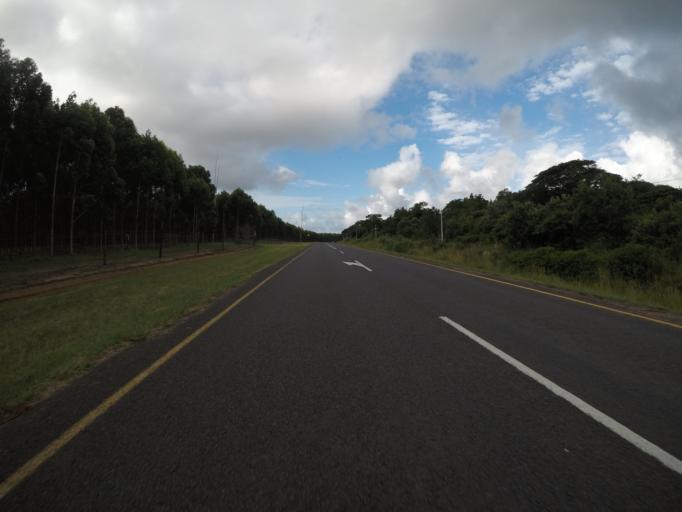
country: ZA
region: KwaZulu-Natal
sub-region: uMkhanyakude District Municipality
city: Mtubatuba
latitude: -28.3733
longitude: 32.2534
